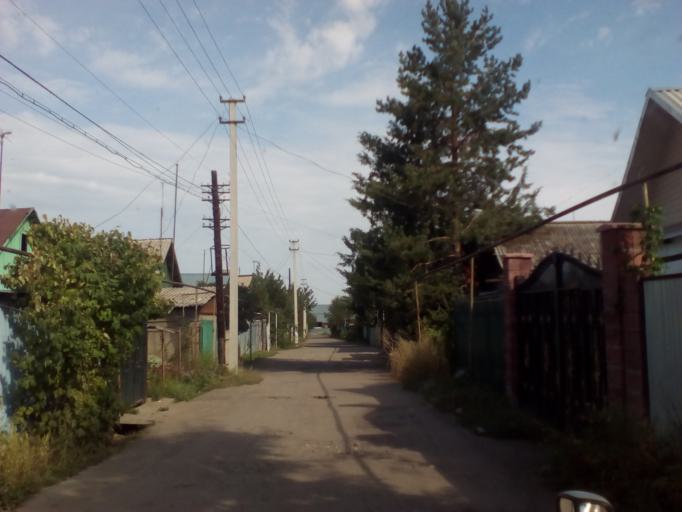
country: KZ
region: Almaty Oblysy
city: Burunday
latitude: 43.1621
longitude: 76.4076
